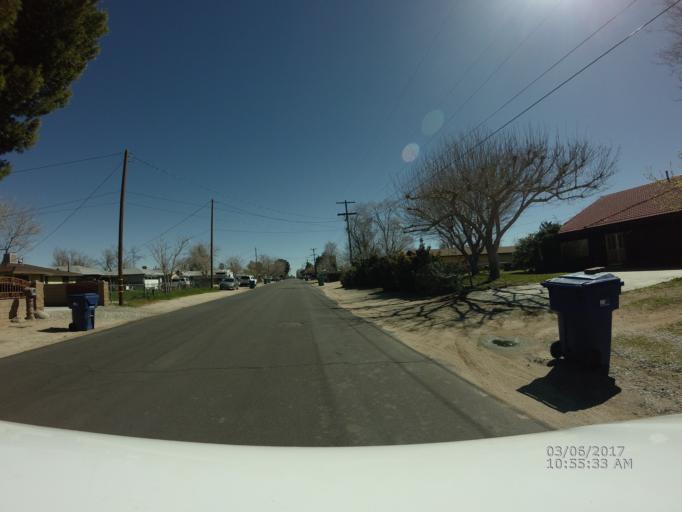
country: US
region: California
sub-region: Los Angeles County
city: Quartz Hill
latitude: 34.6566
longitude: -118.2265
